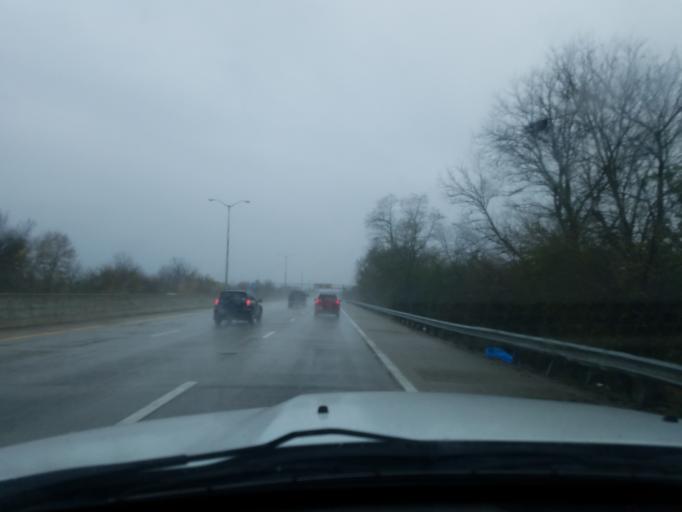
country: US
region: Kentucky
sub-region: Jefferson County
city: Shively
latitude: 38.2399
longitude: -85.8160
